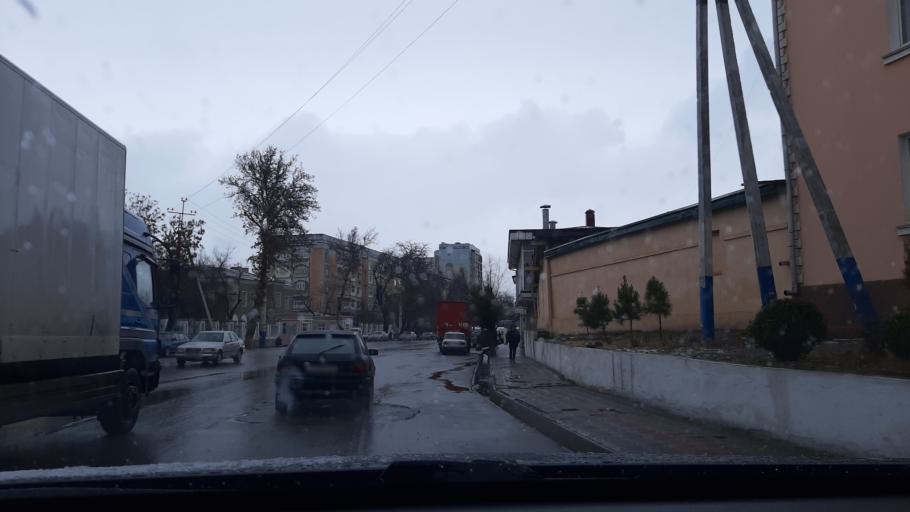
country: TJ
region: Viloyati Sughd
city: Khujand
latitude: 40.2749
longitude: 69.6412
